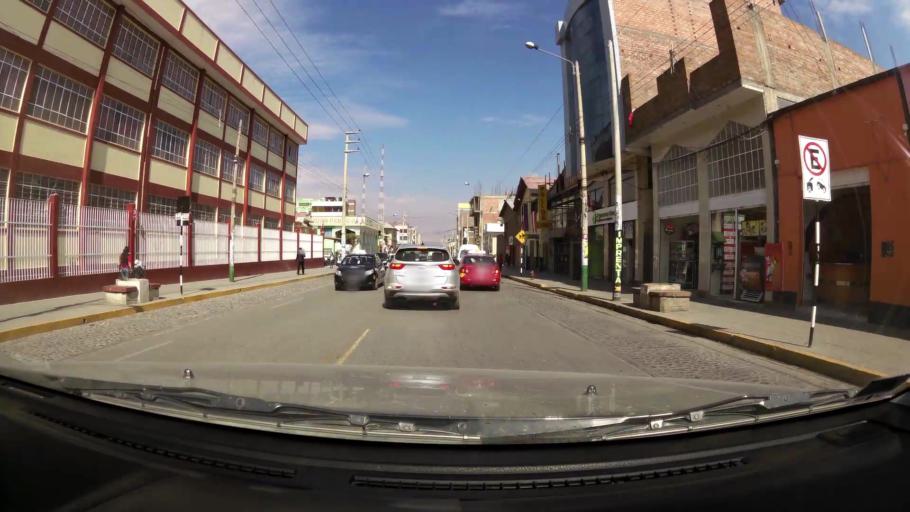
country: PE
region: Junin
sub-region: Provincia de Huancayo
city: El Tambo
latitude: -12.0698
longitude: -75.2123
